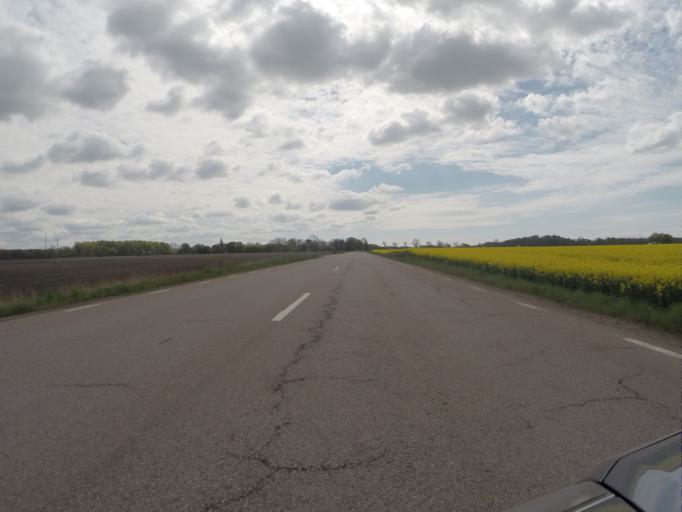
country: SE
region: Skane
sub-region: Helsingborg
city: Hyllinge
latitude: 56.0973
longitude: 12.8022
